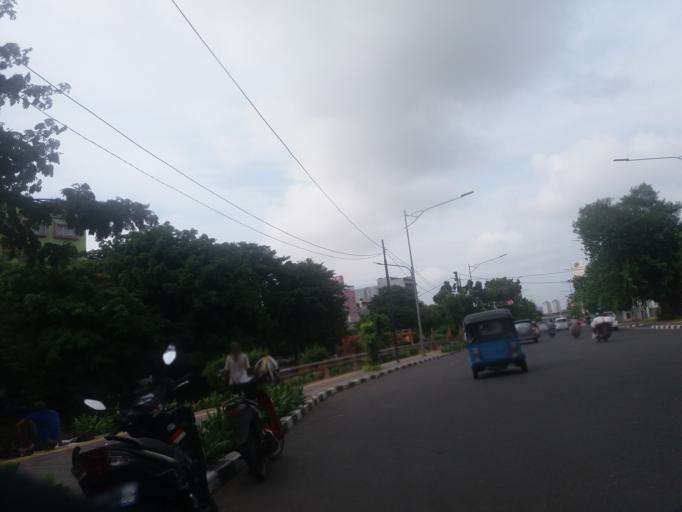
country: ID
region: Jakarta Raya
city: Jakarta
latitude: -6.1675
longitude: 106.8319
